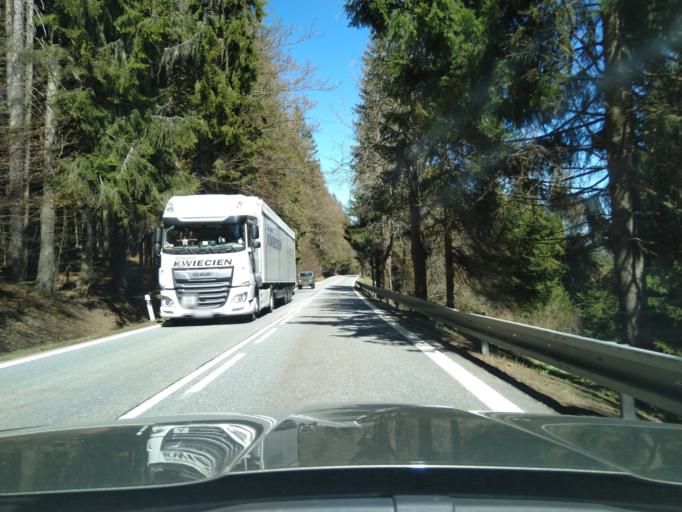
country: CZ
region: Jihocesky
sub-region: Okres Prachatice
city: Vimperk
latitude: 48.9930
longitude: 13.7678
